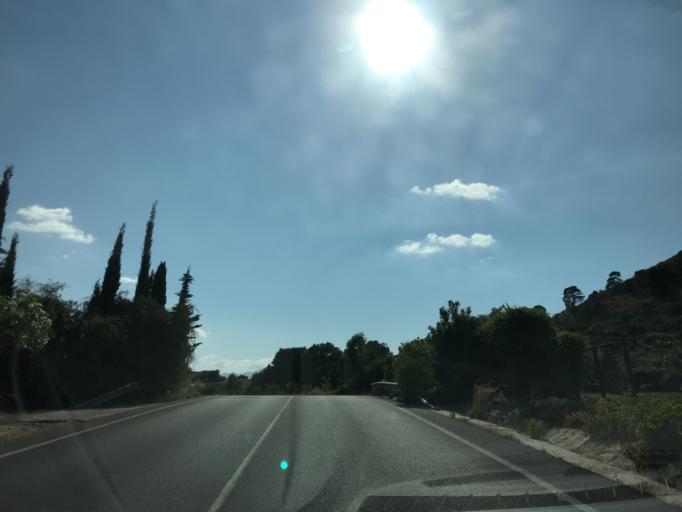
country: ES
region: Andalusia
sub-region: Provincia de Malaga
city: Benahavis
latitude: 36.5077
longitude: -5.0177
